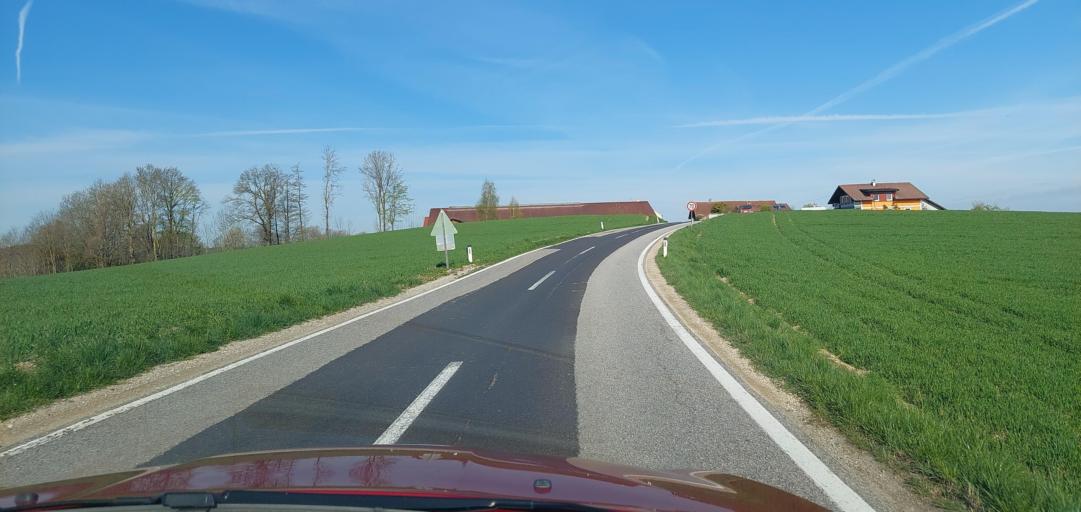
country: AT
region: Upper Austria
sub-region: Politischer Bezirk Ried im Innkreis
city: Ried im Innkreis
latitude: 48.1817
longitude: 13.5200
